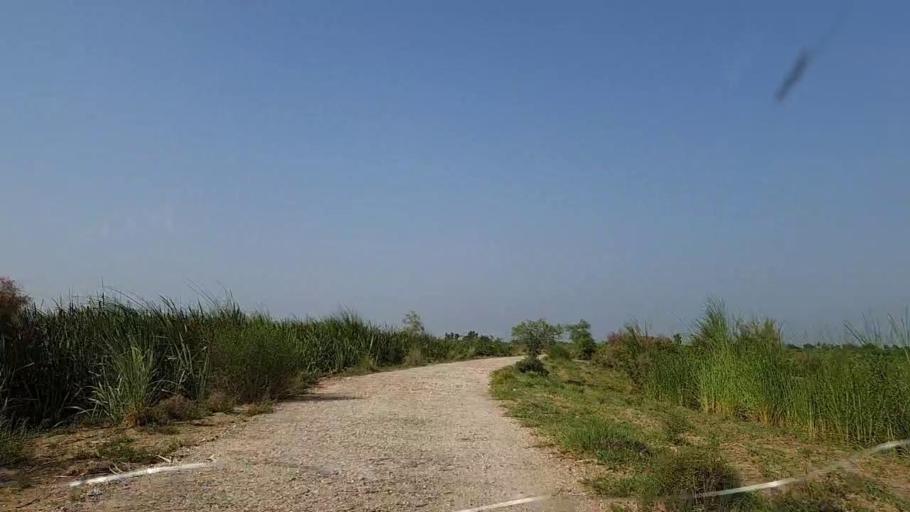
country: PK
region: Sindh
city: Khanpur
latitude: 27.7042
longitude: 69.3862
